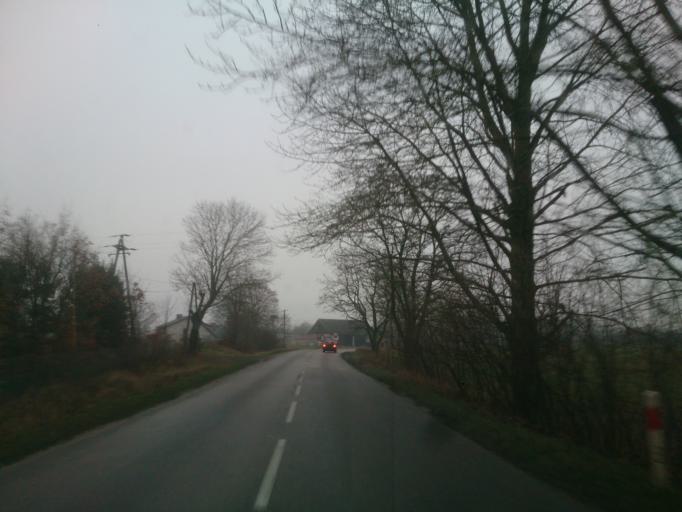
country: PL
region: Pomeranian Voivodeship
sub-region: Powiat koscierski
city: Koscierzyna
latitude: 54.0562
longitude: 18.0328
